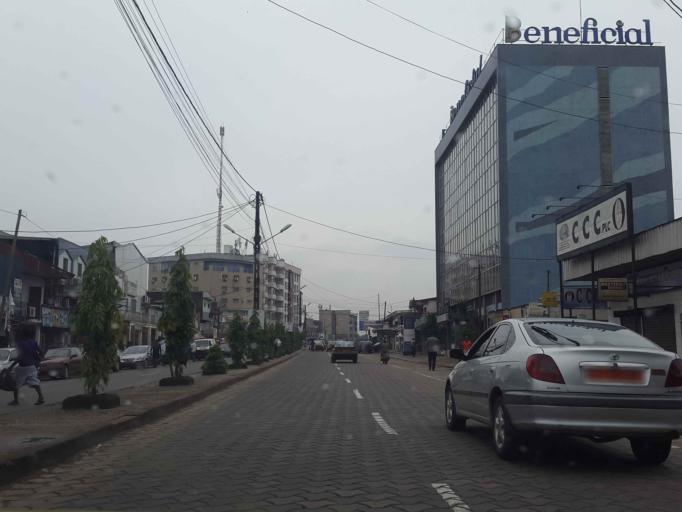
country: CM
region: Littoral
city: Douala
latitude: 4.0523
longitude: 9.7038
